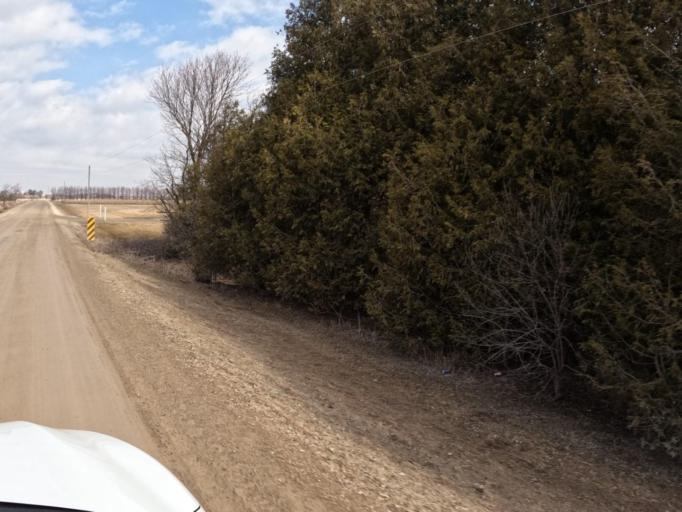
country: CA
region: Ontario
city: Orangeville
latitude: 43.9209
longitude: -80.2395
